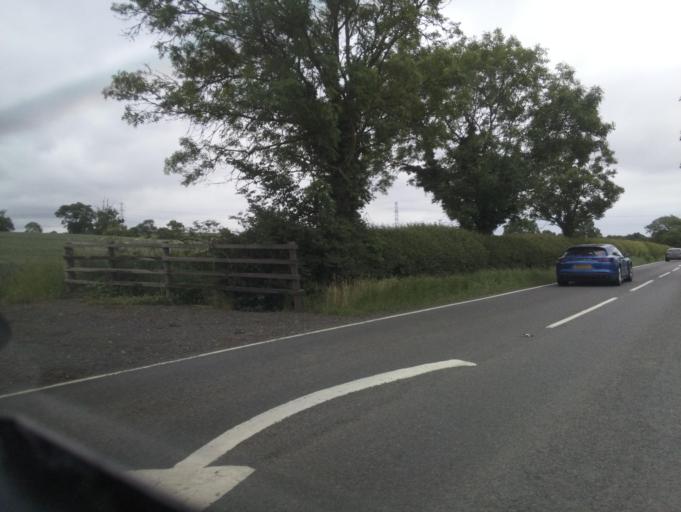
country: GB
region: England
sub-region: Leicestershire
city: Grimston
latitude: 52.7685
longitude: -0.9717
